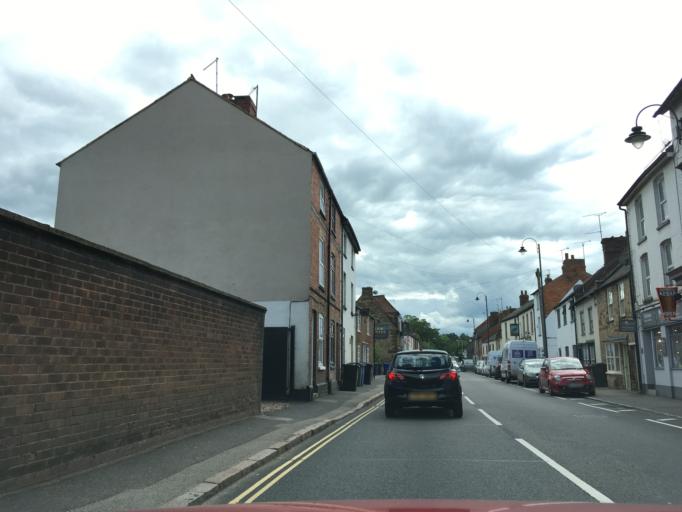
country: GB
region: England
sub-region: Northamptonshire
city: Towcester
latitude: 52.1302
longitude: -0.9864
